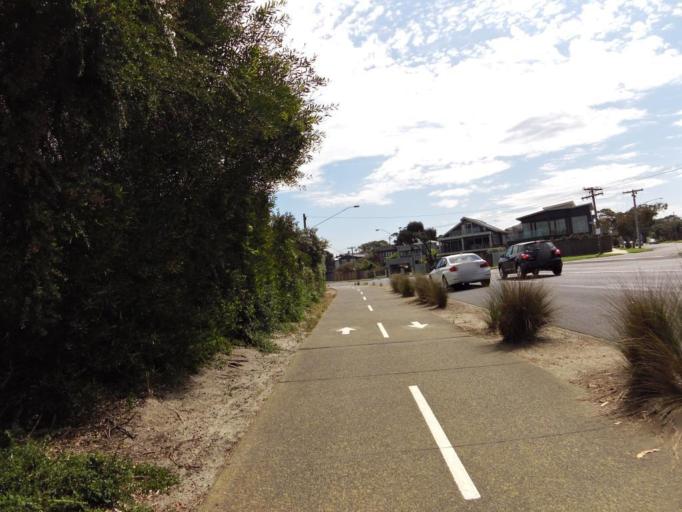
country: AU
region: Victoria
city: Beaumaris
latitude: -37.9883
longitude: 145.0277
